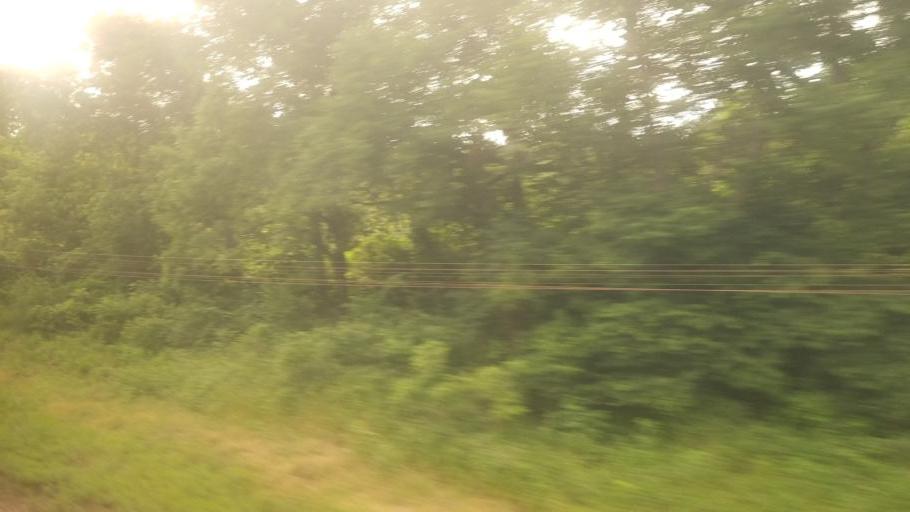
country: US
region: Kansas
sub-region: Osage County
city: Carbondale
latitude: 38.8650
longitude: -95.6971
